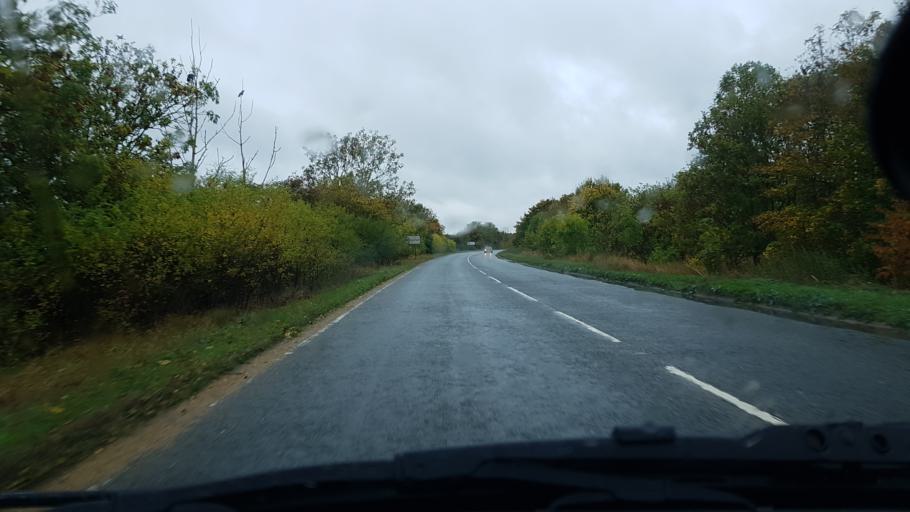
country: GB
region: England
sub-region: Oxfordshire
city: Ducklington
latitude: 51.7655
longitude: -1.4870
